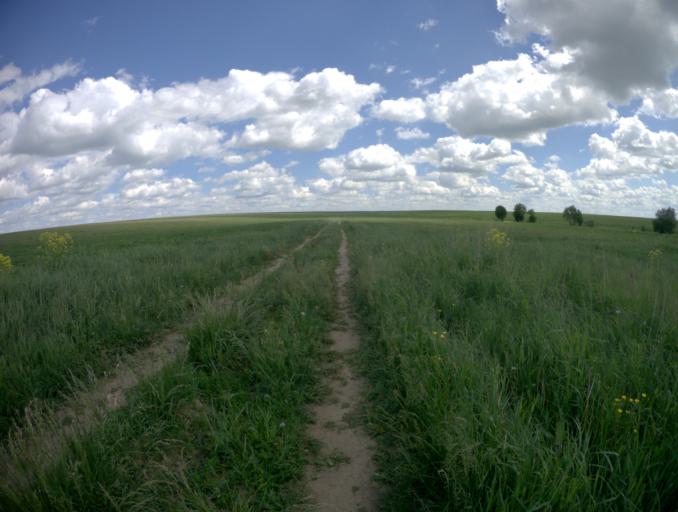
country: RU
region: Ivanovo
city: Gavrilov Posad
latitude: 56.4393
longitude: 40.2581
